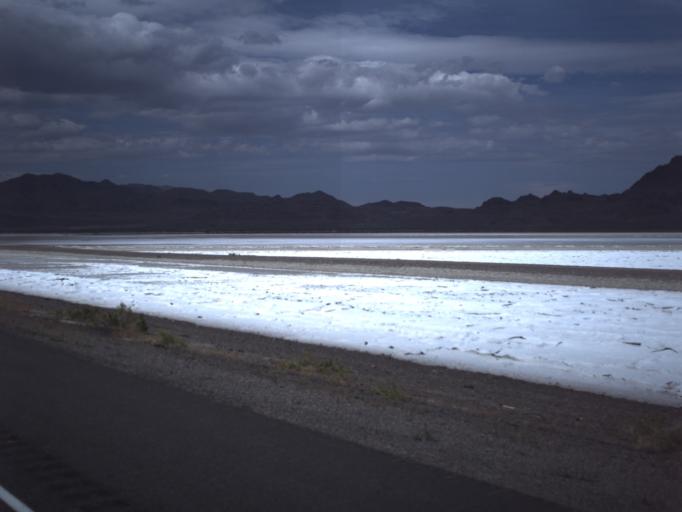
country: US
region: Utah
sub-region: Tooele County
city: Wendover
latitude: 40.7410
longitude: -113.9346
